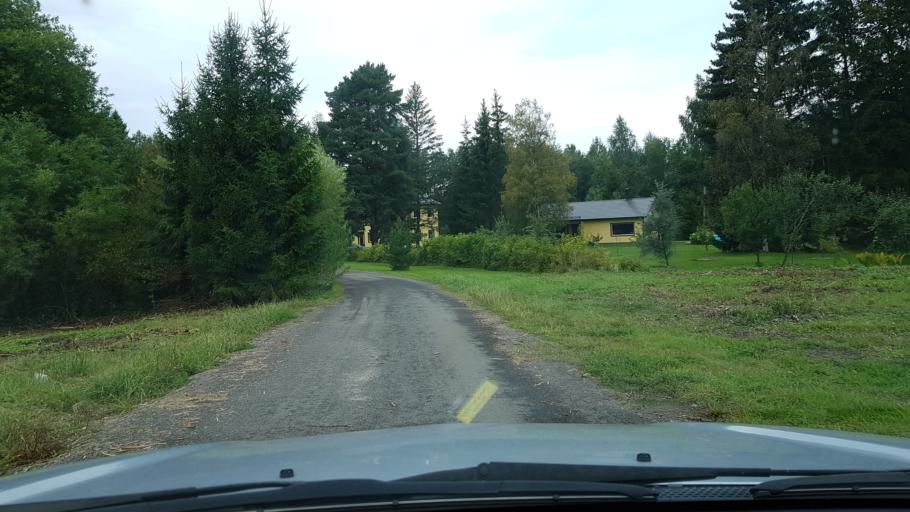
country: EE
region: Harju
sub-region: Rae vald
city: Jueri
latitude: 59.3720
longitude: 24.9485
